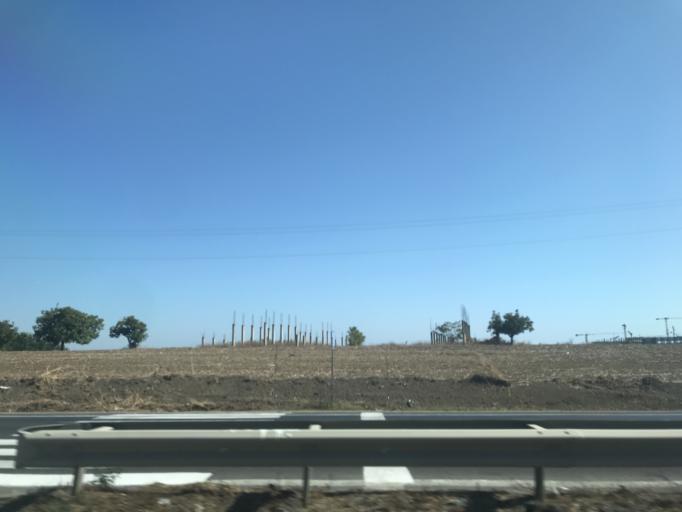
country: TR
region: Tekirdag
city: Tekirdag
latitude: 41.0143
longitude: 27.5172
